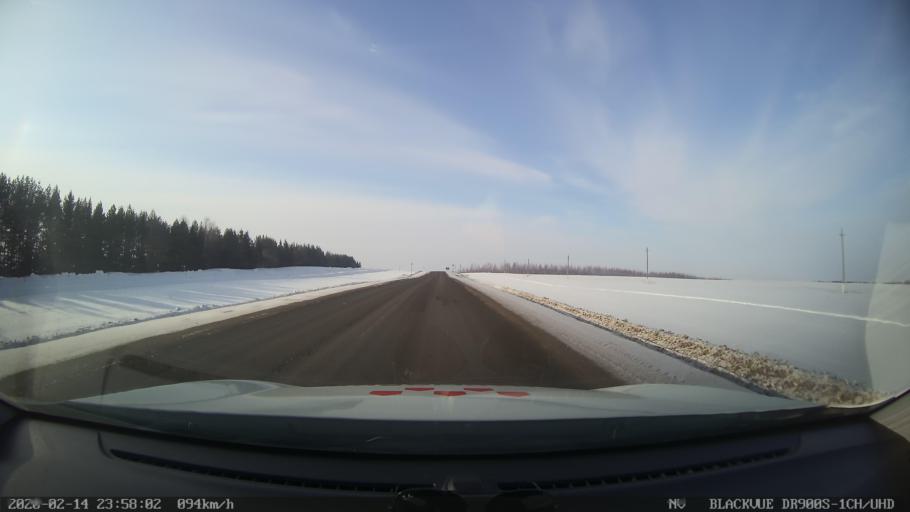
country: RU
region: Tatarstan
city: Kuybyshevskiy Zaton
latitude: 55.3379
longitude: 49.0965
